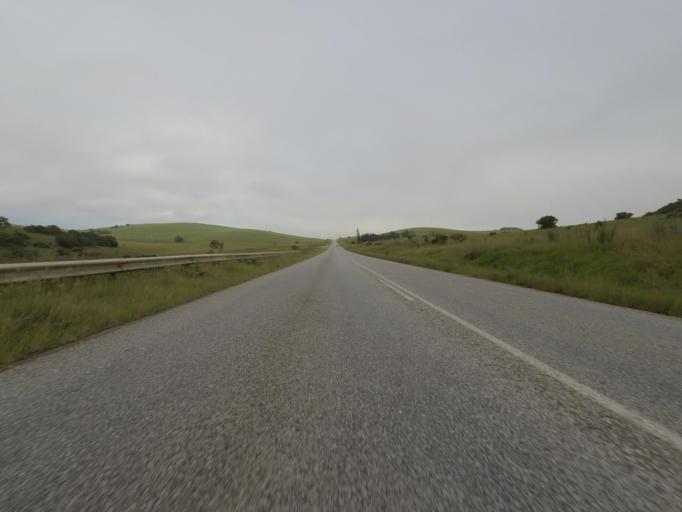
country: ZA
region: Eastern Cape
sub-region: Cacadu District Municipality
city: Port Alfred
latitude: -33.6092
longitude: 26.8123
